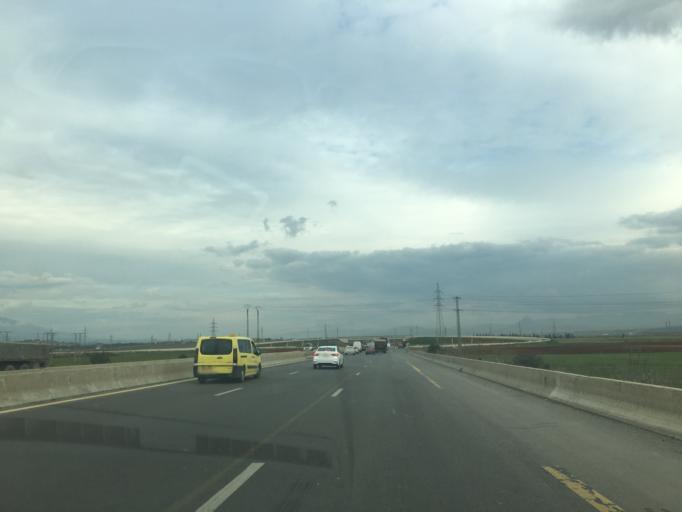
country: DZ
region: Bouira
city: Bouira
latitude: 36.3309
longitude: 3.9386
